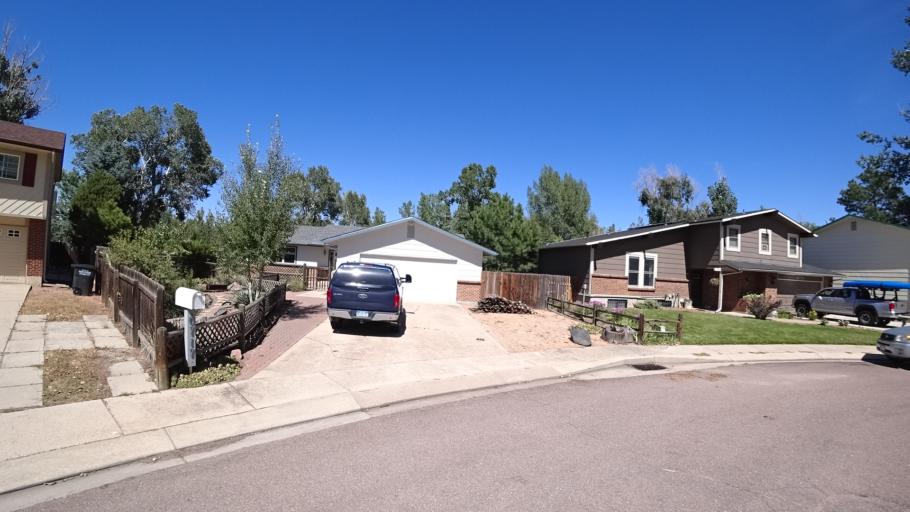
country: US
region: Colorado
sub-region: El Paso County
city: Air Force Academy
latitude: 38.9290
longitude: -104.7916
